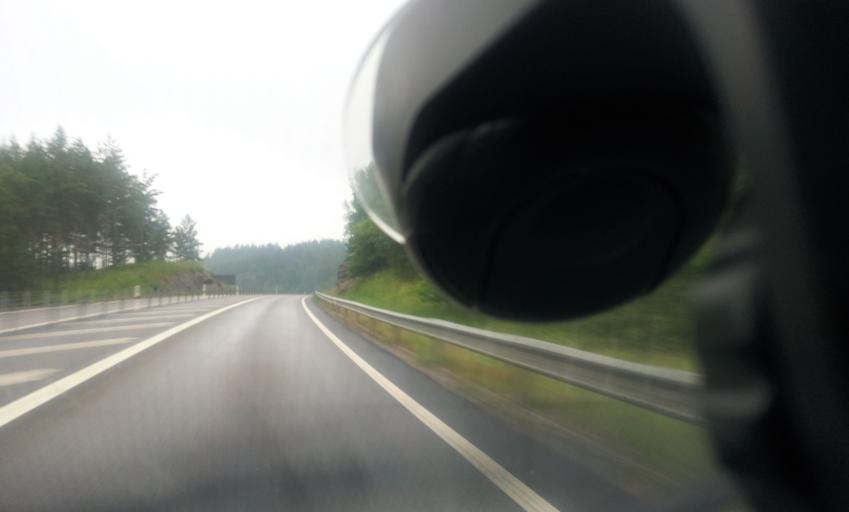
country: SE
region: Kalmar
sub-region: Vasterviks Kommun
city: Gamleby
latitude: 57.8998
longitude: 16.3836
